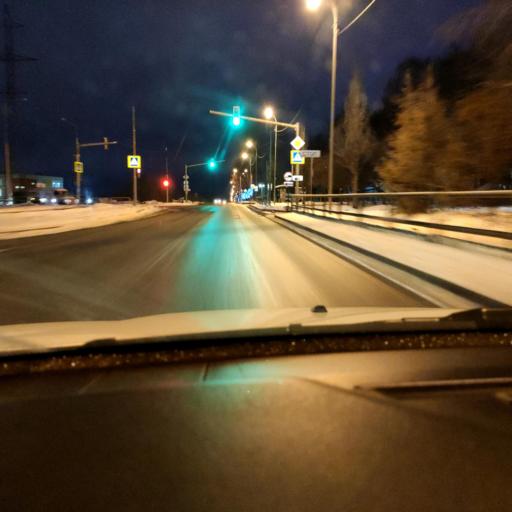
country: RU
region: Samara
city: Petra-Dubrava
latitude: 53.3085
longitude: 50.2775
